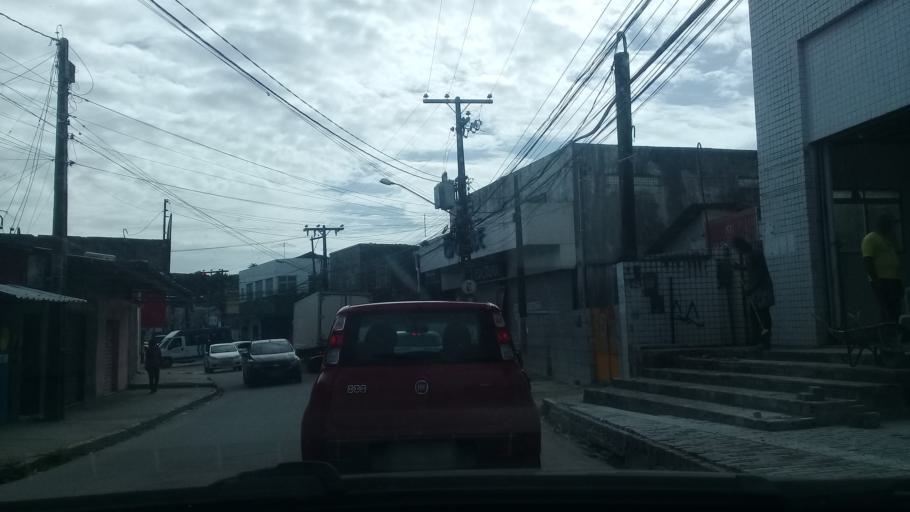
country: BR
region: Pernambuco
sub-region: Jaboatao Dos Guararapes
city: Jaboatao dos Guararapes
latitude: -8.0906
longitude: -34.9731
